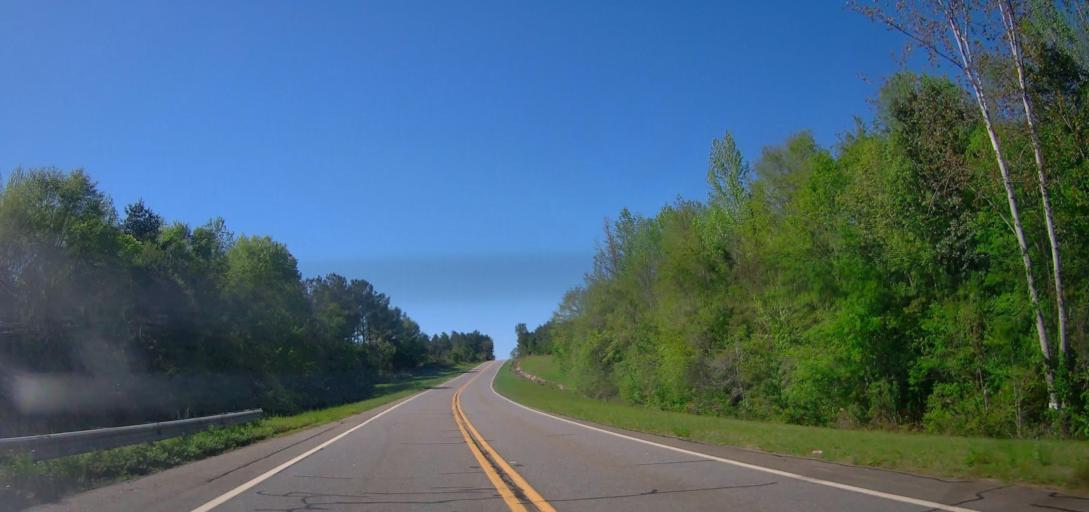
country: US
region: Georgia
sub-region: Dooly County
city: Unadilla
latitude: 32.2471
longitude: -83.6134
